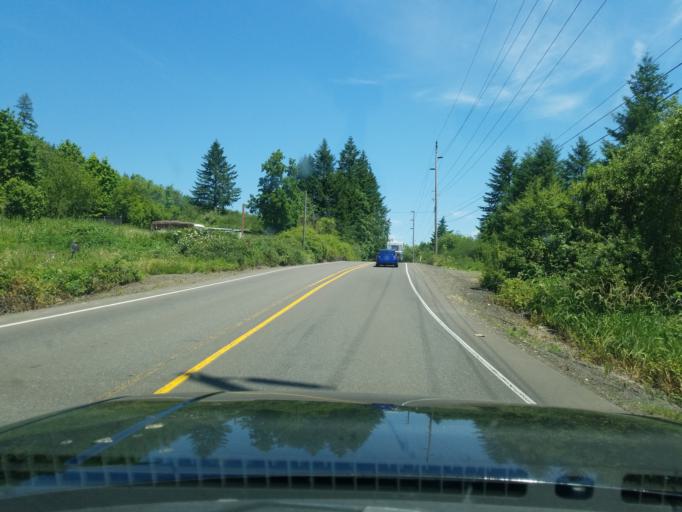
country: US
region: Oregon
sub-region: Yamhill County
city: Yamhill
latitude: 45.3869
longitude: -123.1386
